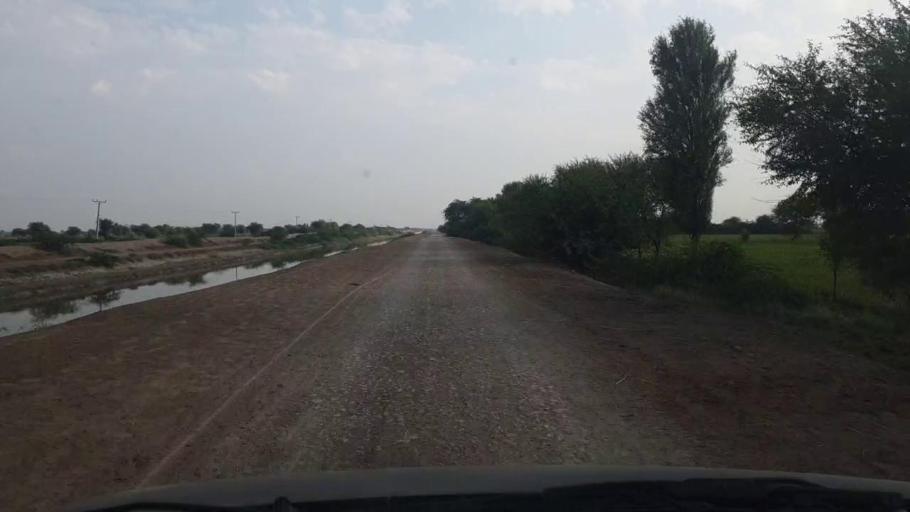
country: PK
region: Sindh
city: Badin
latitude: 24.5203
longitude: 68.6826
